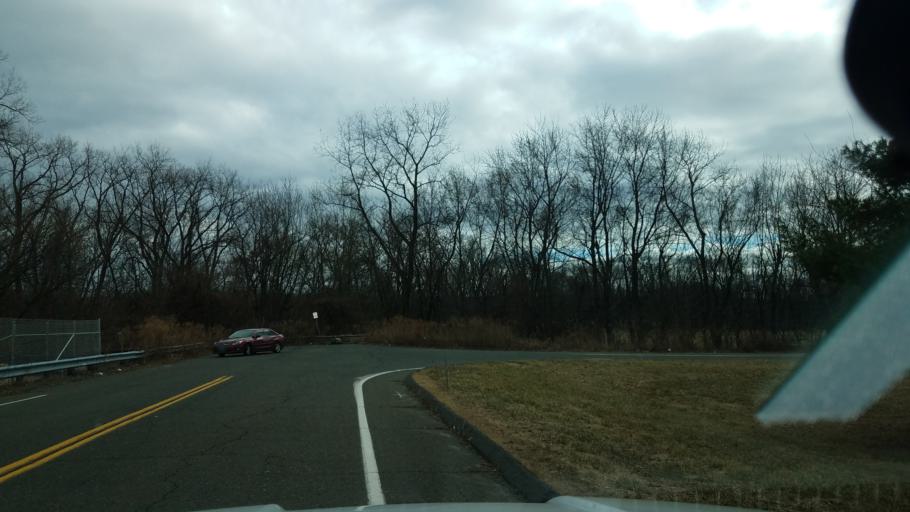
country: US
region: Connecticut
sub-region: Hartford County
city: Wethersfield
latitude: 41.7114
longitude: -72.6421
